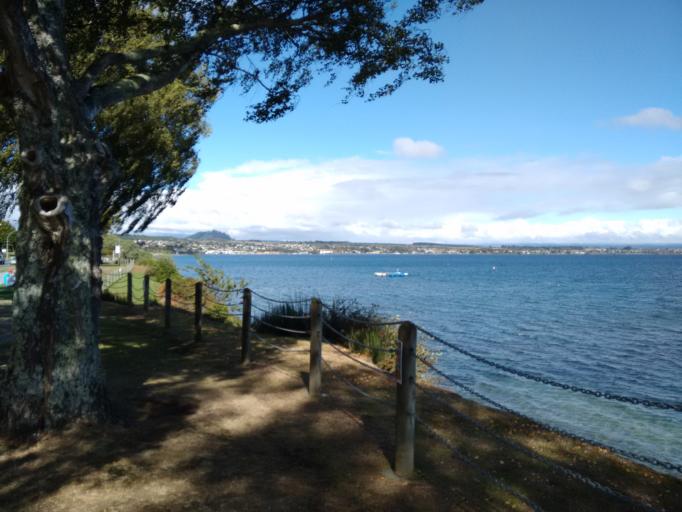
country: NZ
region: Waikato
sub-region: Taupo District
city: Taupo
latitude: -38.6905
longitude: 176.0705
